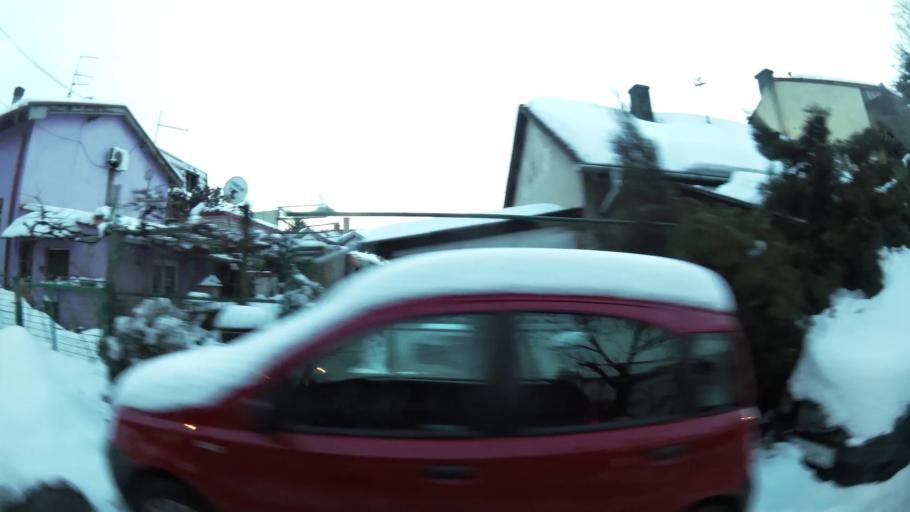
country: RS
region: Central Serbia
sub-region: Belgrade
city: Palilula
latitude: 44.7968
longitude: 20.5085
